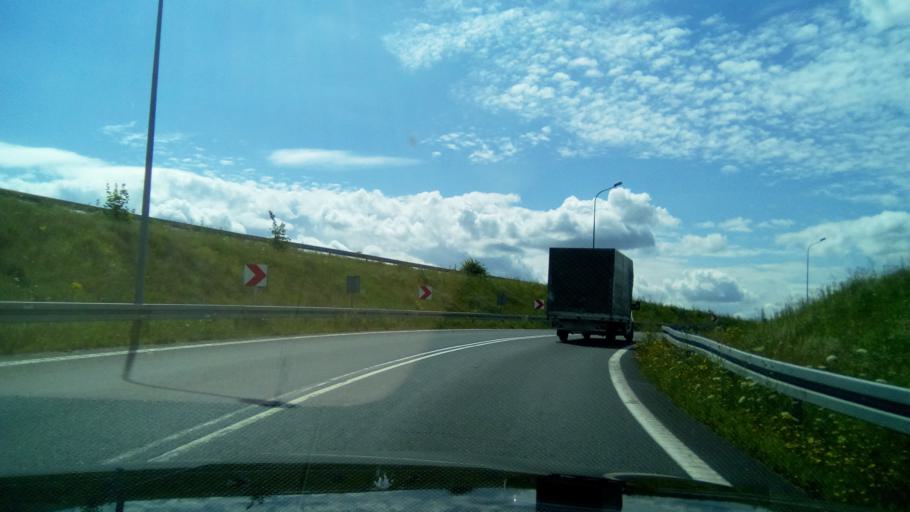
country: PL
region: Kujawsko-Pomorskie
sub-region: Powiat nakielski
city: Szubin
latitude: 53.0204
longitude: 17.7713
